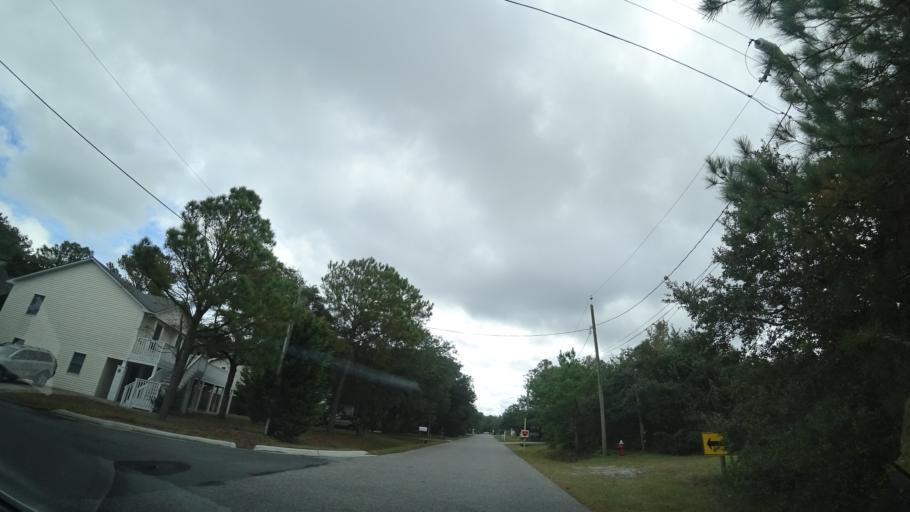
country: US
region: North Carolina
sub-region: Dare County
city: Kill Devil Hills
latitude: 36.0040
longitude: -75.6601
